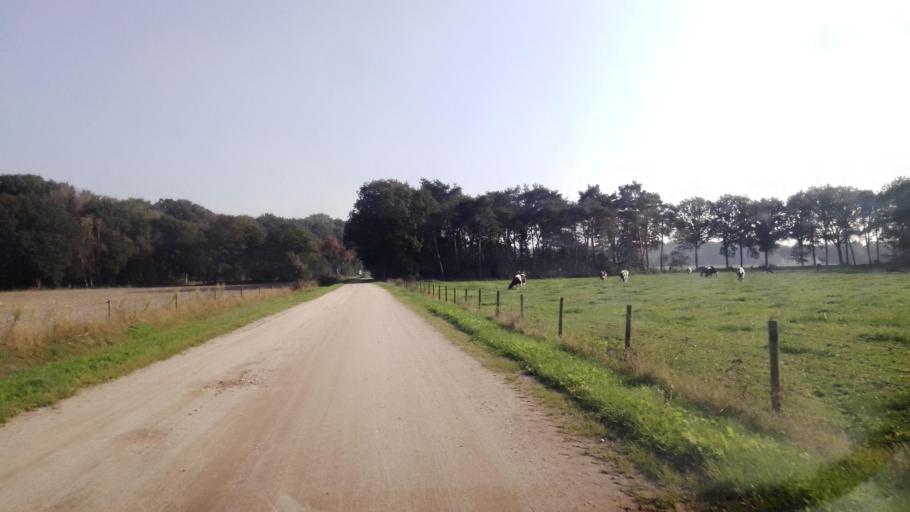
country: NL
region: Limburg
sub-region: Gemeente Venlo
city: Tegelen
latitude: 51.3101
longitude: 6.1394
